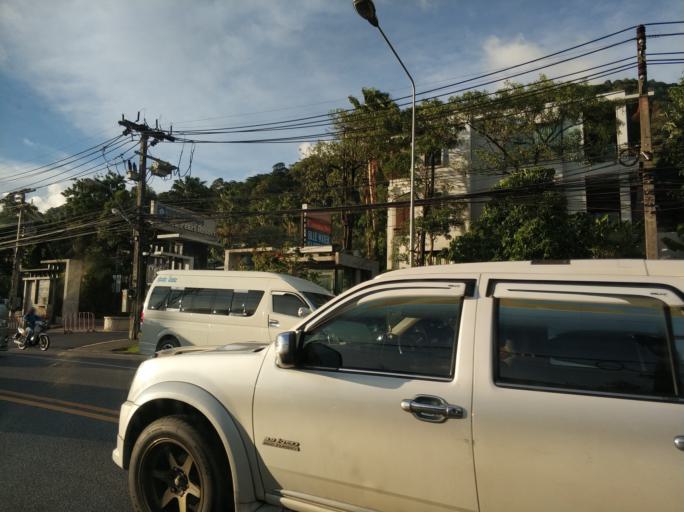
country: TH
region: Phuket
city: Patong
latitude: 7.9037
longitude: 98.3136
